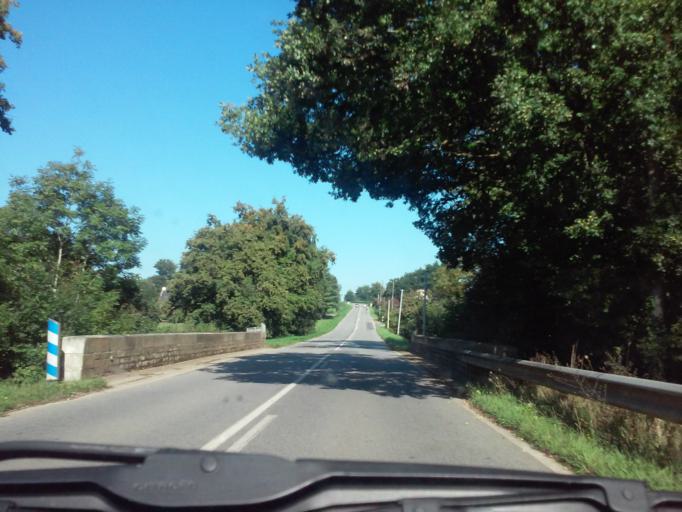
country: FR
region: Brittany
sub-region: Departement d'Ille-et-Vilaine
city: Chevaigne
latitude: 48.1963
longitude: -1.6250
